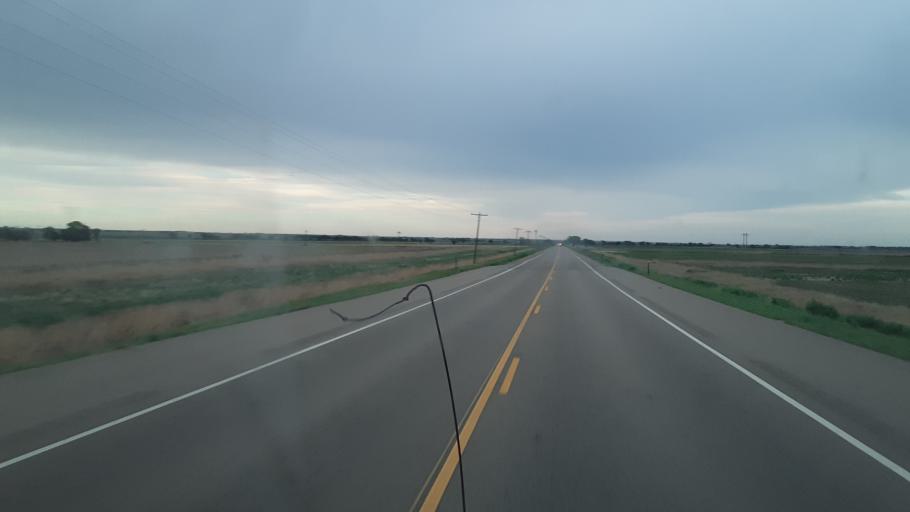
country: US
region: Colorado
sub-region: Prowers County
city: Lamar
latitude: 38.0526
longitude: -102.2516
